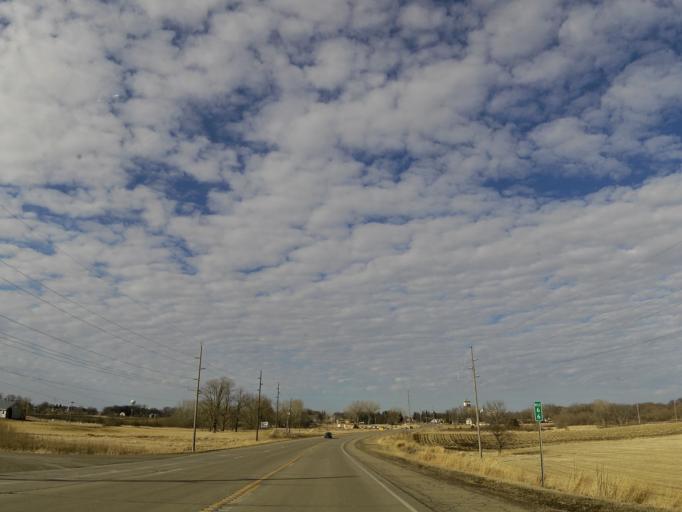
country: US
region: Minnesota
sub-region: Le Sueur County
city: New Prague
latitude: 44.5331
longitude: -93.5856
